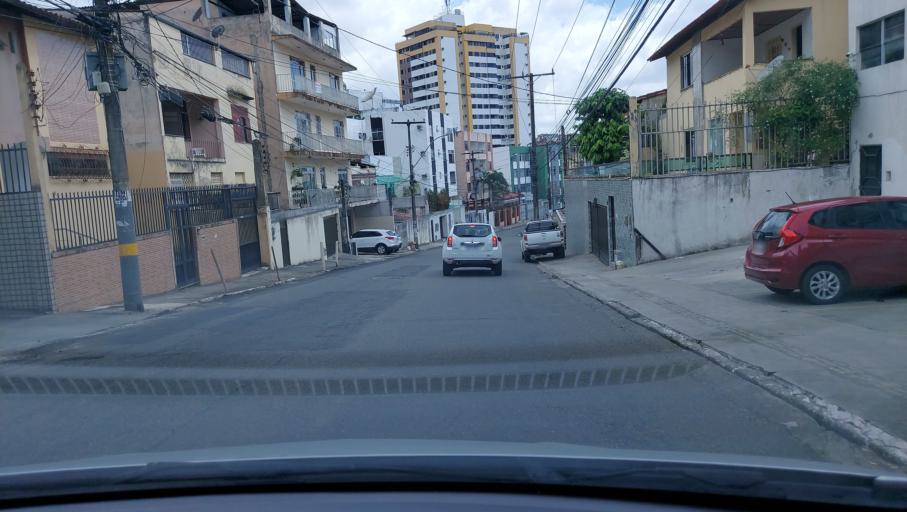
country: BR
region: Bahia
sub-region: Salvador
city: Salvador
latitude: -12.9699
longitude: -38.4897
